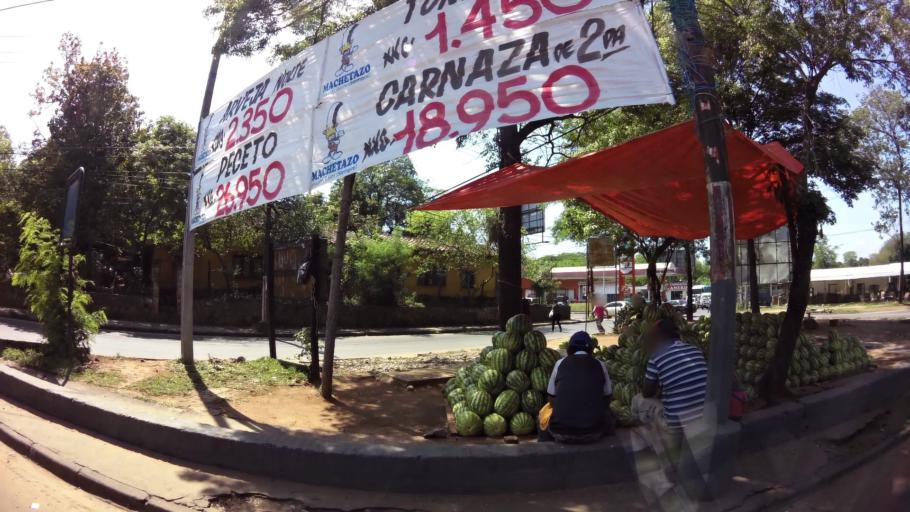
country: PY
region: Central
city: San Lorenzo
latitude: -25.3368
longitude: -57.5102
